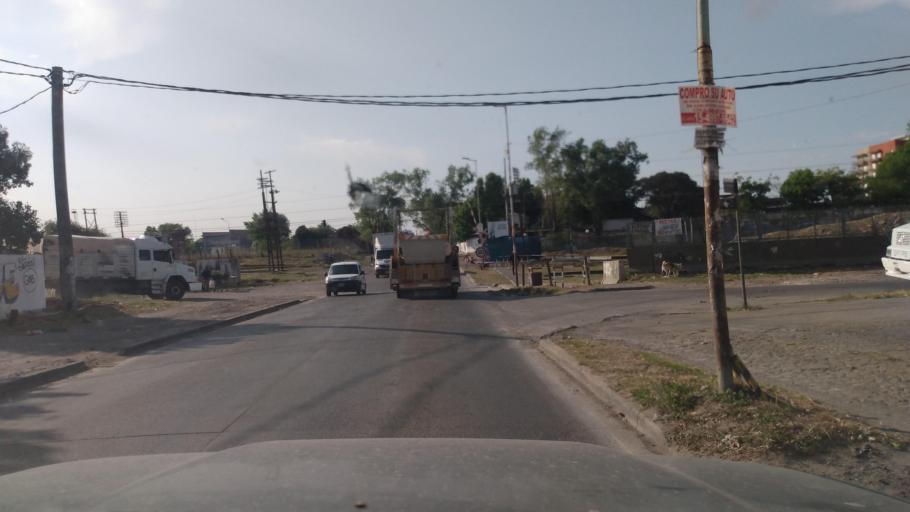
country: AR
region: Buenos Aires
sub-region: Partido de Moron
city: Moron
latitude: -34.6462
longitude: -58.6099
